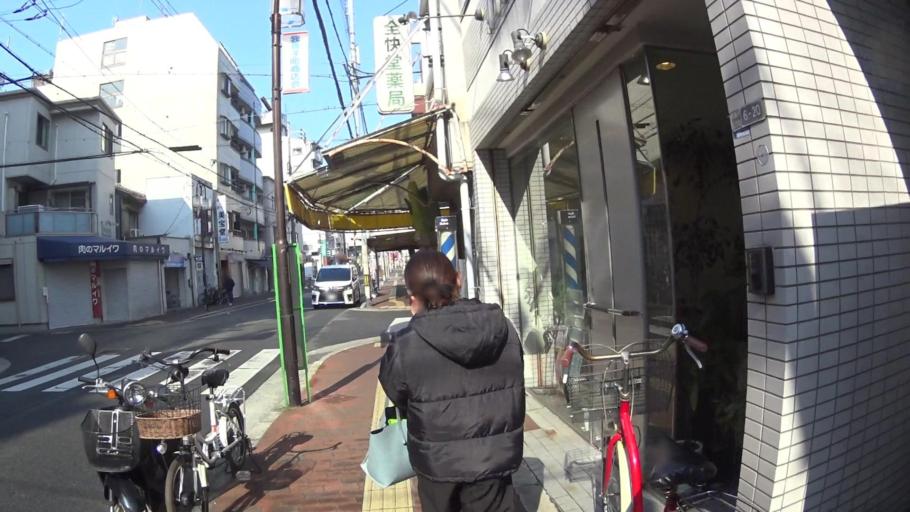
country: JP
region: Osaka
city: Sakai
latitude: 34.6010
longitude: 135.5078
